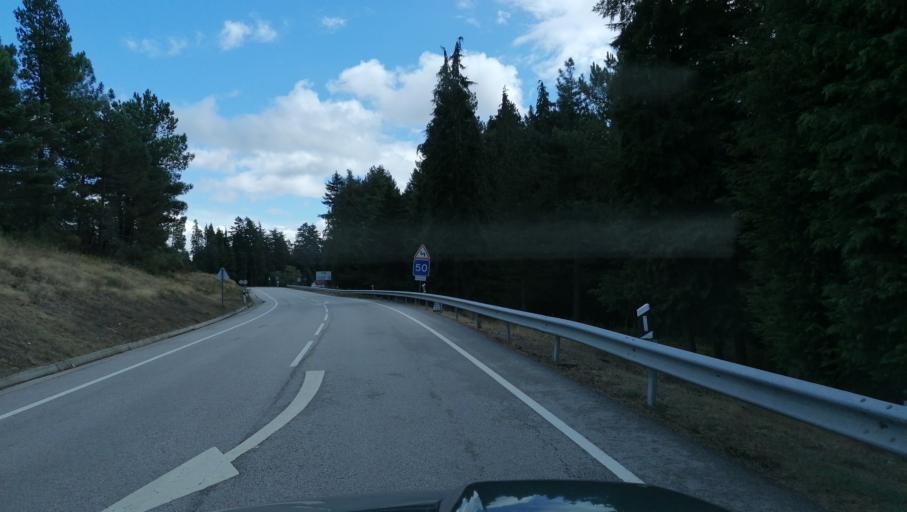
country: PT
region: Vila Real
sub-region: Vila Pouca de Aguiar
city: Vila Pouca de Aguiar
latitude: 41.5166
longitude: -7.6022
